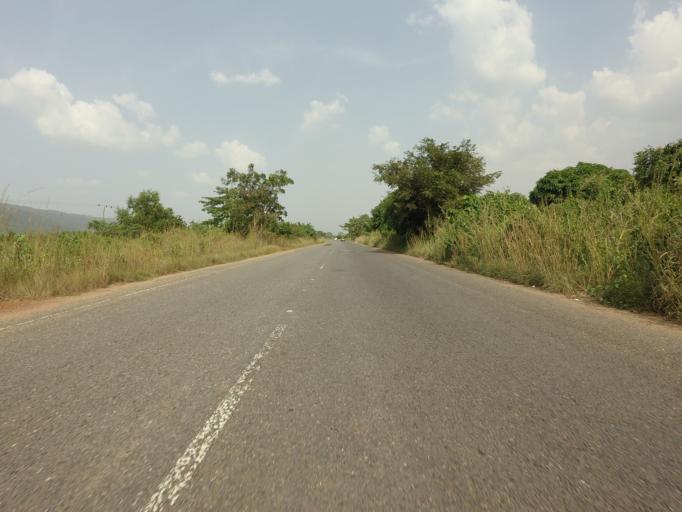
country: GH
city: Akropong
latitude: 5.9346
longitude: -0.0331
